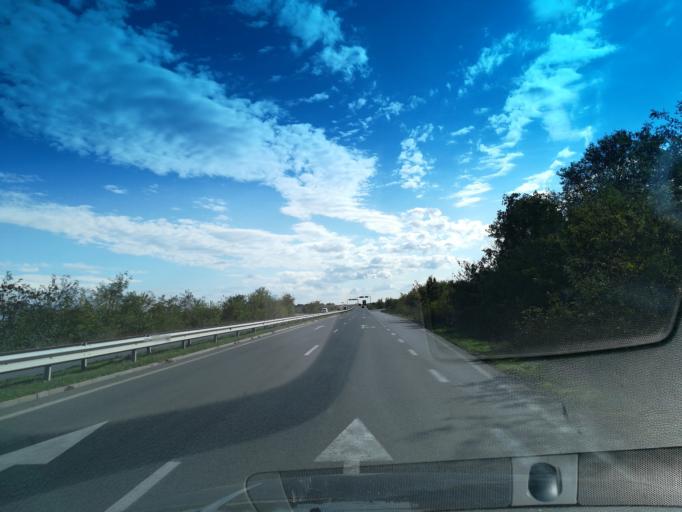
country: BG
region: Stara Zagora
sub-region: Obshtina Stara Zagora
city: Stara Zagora
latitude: 42.3443
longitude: 25.6605
